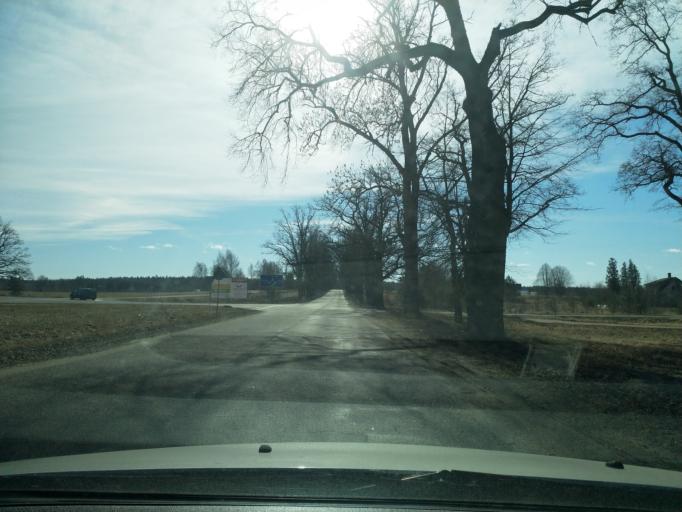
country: LV
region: Valmieras Rajons
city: Valmiera
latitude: 57.5190
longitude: 25.4197
